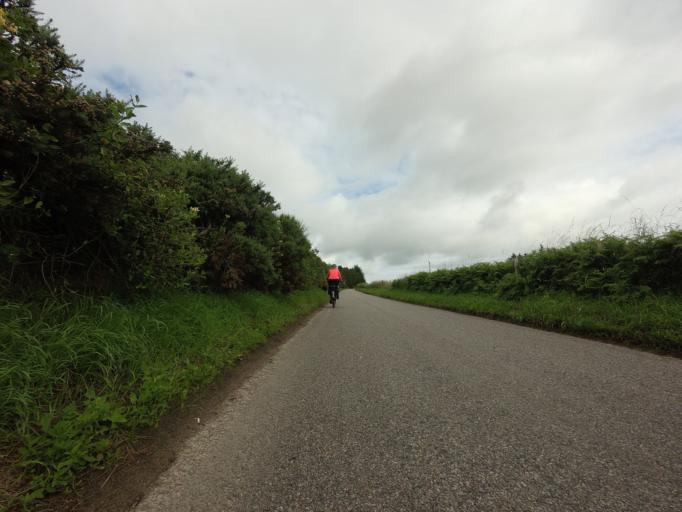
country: GB
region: Scotland
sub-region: Moray
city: Elgin
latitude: 57.6581
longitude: -3.3529
